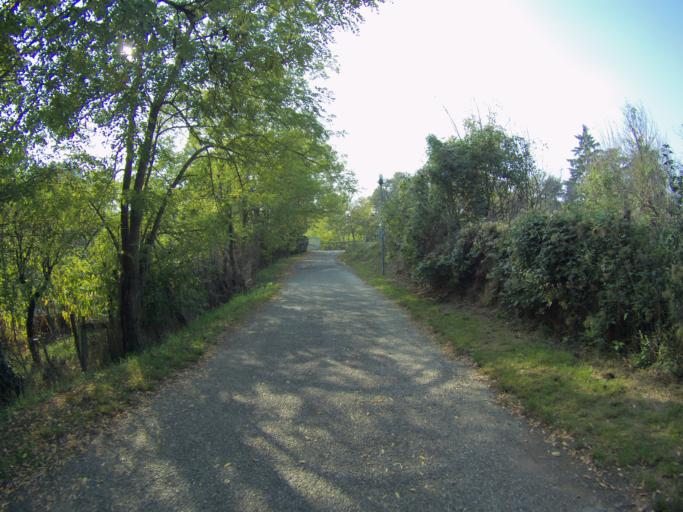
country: IT
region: Emilia-Romagna
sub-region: Provincia di Reggio Emilia
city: Reggio nell'Emilia
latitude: 44.6742
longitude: 10.6232
